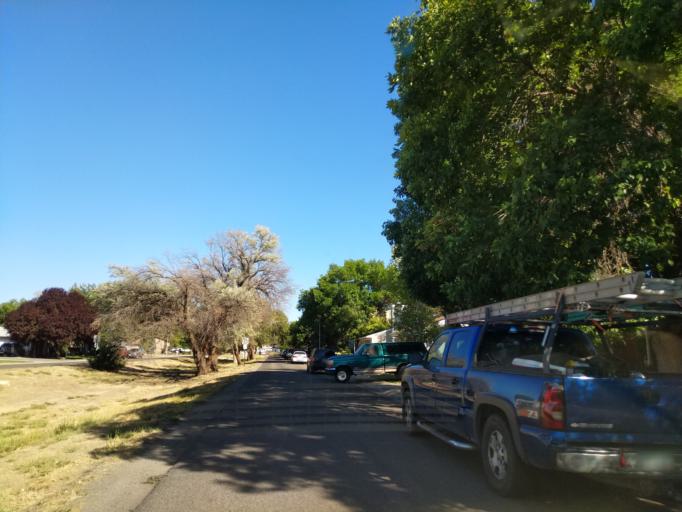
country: US
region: Colorado
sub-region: Mesa County
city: Orchard Mesa
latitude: 39.0433
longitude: -108.5268
